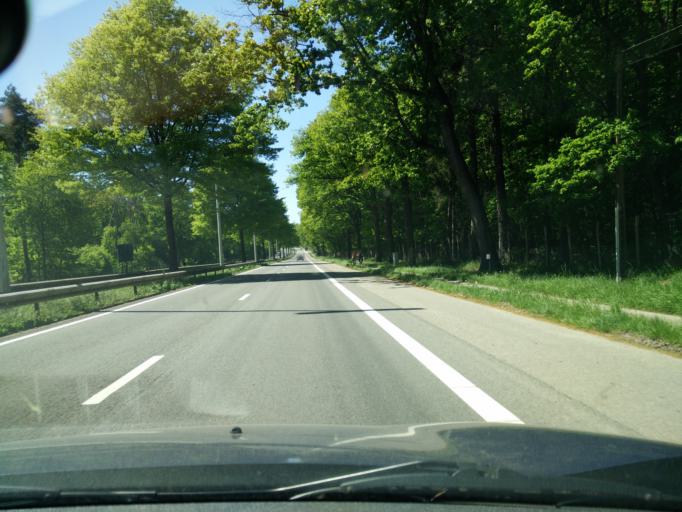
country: BE
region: Flanders
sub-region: Provincie Limburg
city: Maasmechelen
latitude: 51.0158
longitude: 5.6847
